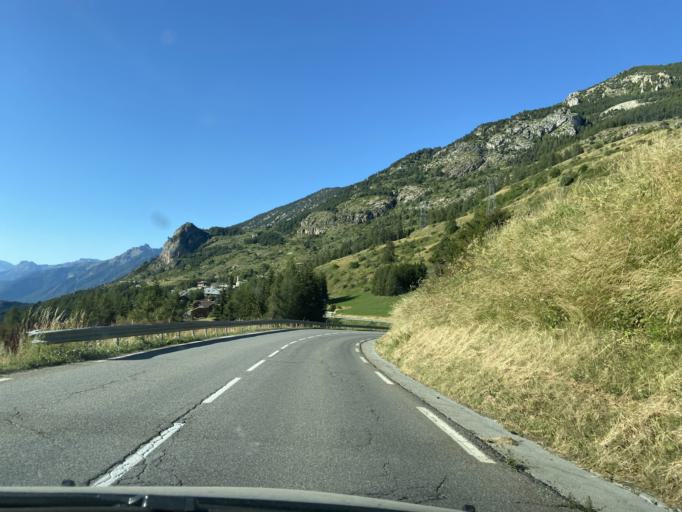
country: FR
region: Provence-Alpes-Cote d'Azur
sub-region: Departement des Hautes-Alpes
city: Guillestre
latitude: 44.6039
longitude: 6.6887
